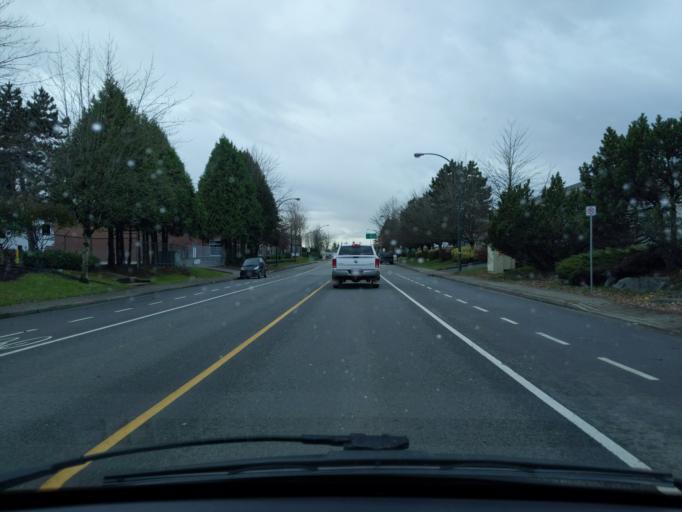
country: CA
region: British Columbia
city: Pitt Meadows
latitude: 49.2094
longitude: -122.6639
